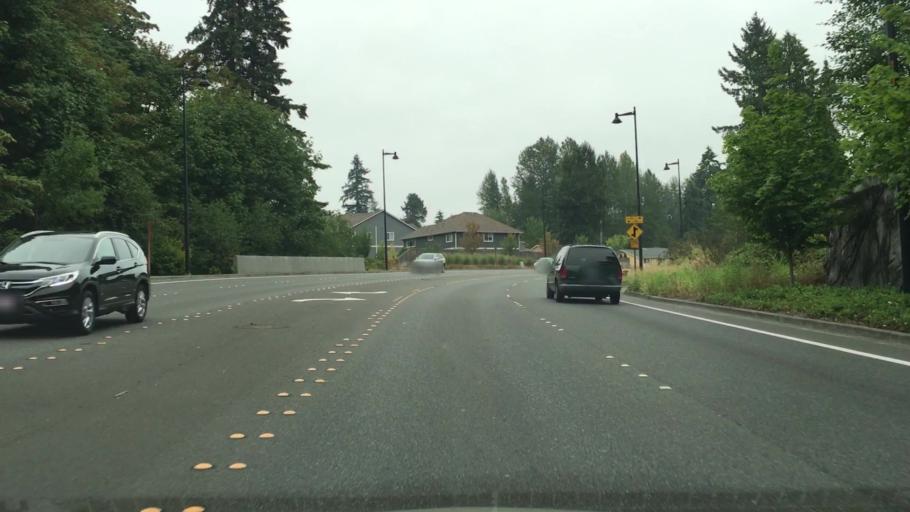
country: US
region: Washington
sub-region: King County
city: Newcastle
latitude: 47.5146
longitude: -122.1570
